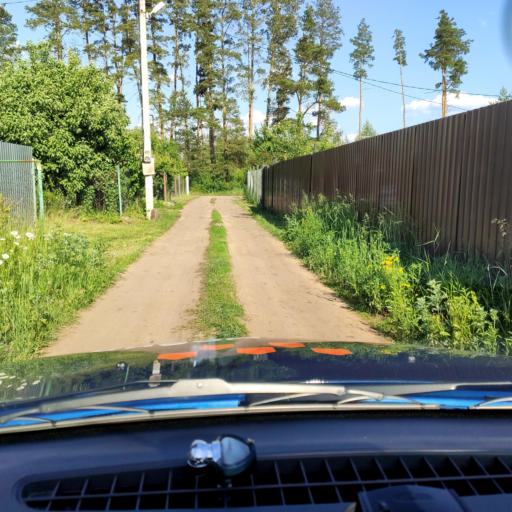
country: RU
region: Voronezj
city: Ramon'
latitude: 51.8930
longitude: 39.2061
